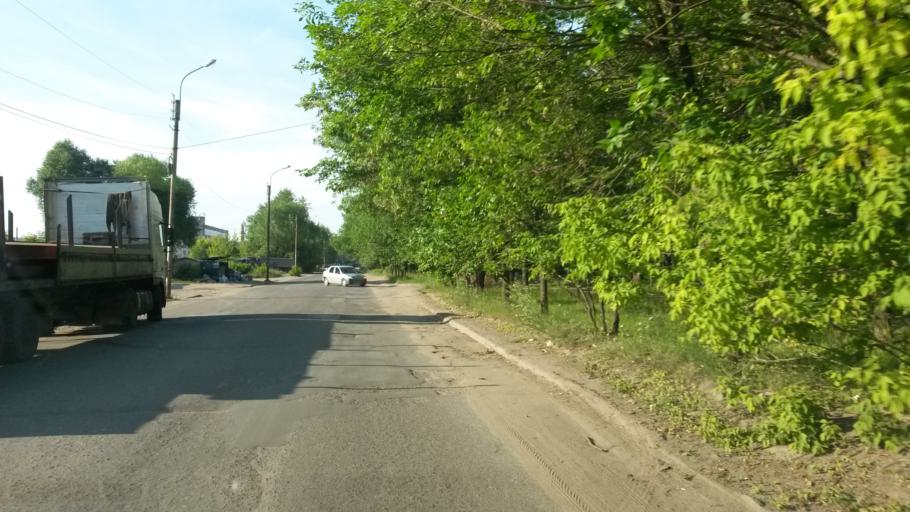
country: RU
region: Ivanovo
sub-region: Gorod Ivanovo
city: Ivanovo
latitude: 56.9591
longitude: 40.9850
